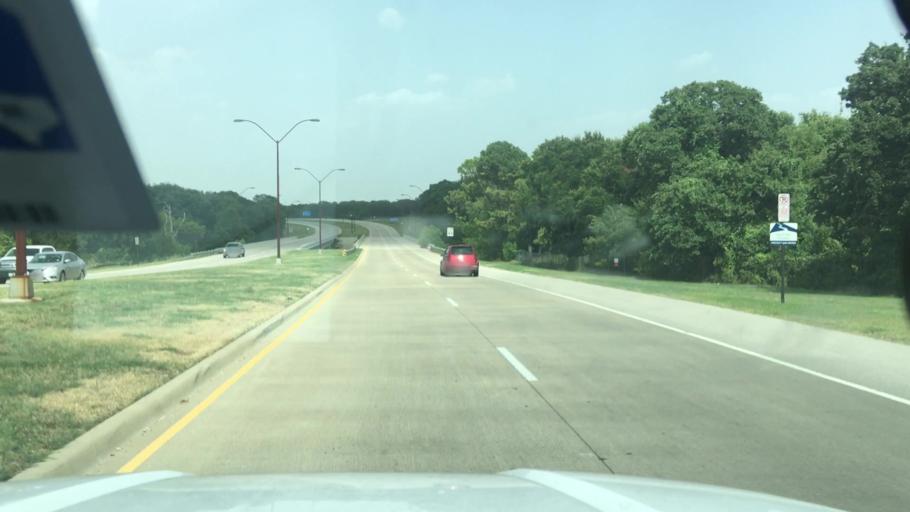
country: US
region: Texas
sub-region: Tarrant County
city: Euless
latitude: 32.8671
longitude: -97.0626
